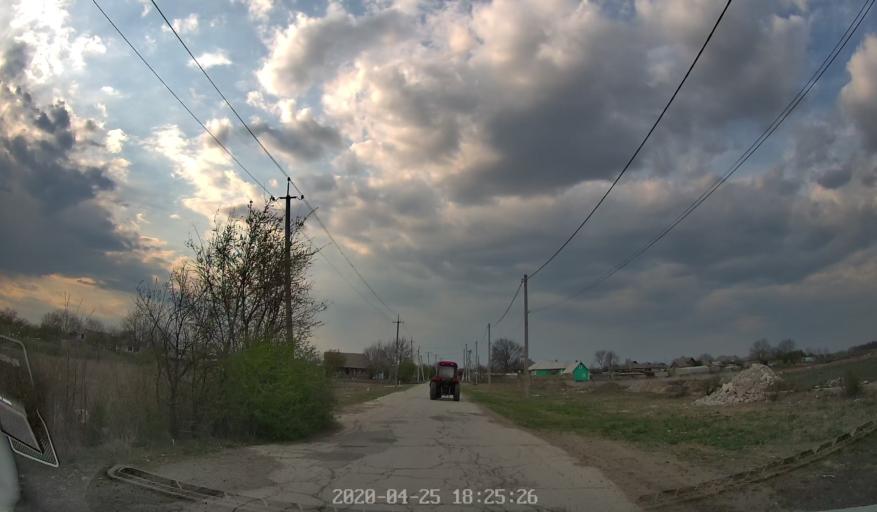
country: MD
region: Criuleni
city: Criuleni
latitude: 47.1618
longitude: 29.1290
